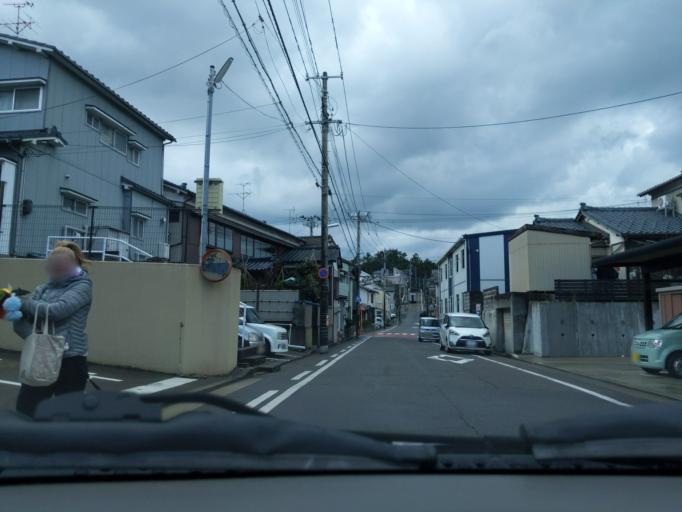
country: JP
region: Niigata
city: Niigata-shi
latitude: 37.9297
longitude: 139.0431
